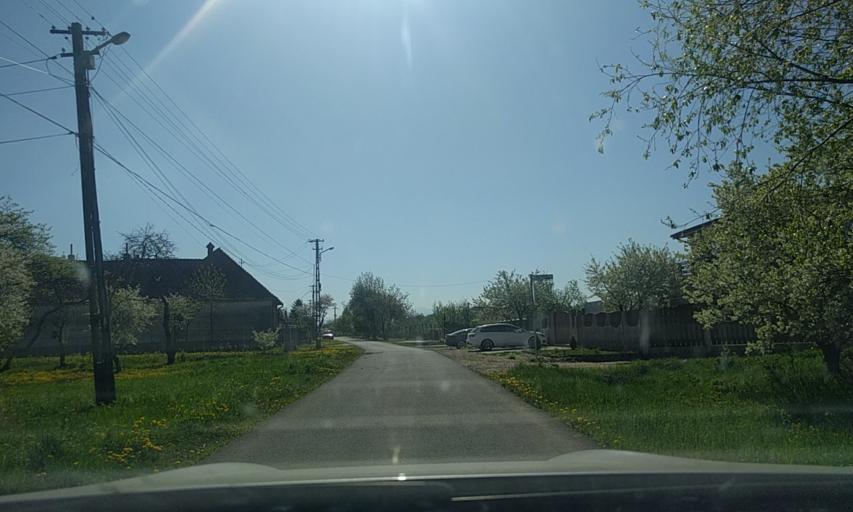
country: RO
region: Brasov
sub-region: Comuna Bod
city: Colonia Bod
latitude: 45.7158
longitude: 25.5735
